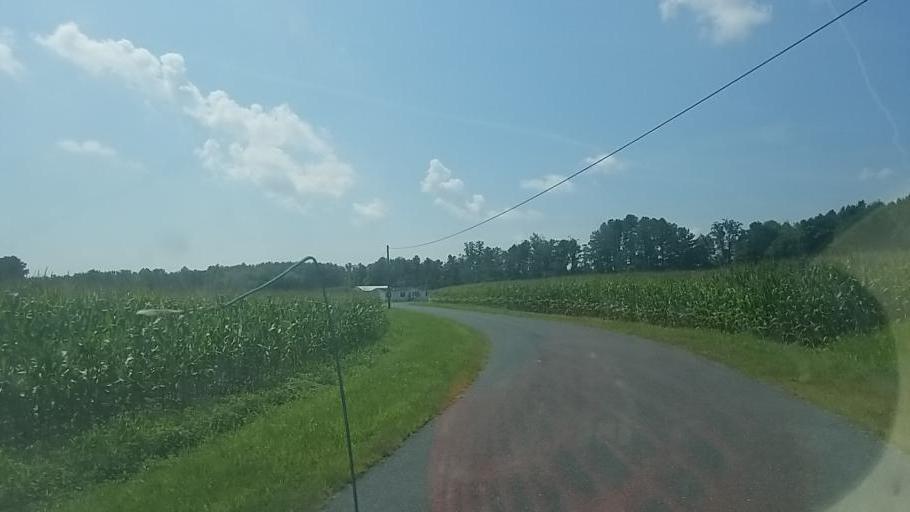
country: US
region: Maryland
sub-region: Worcester County
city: Berlin
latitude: 38.2918
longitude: -75.2959
